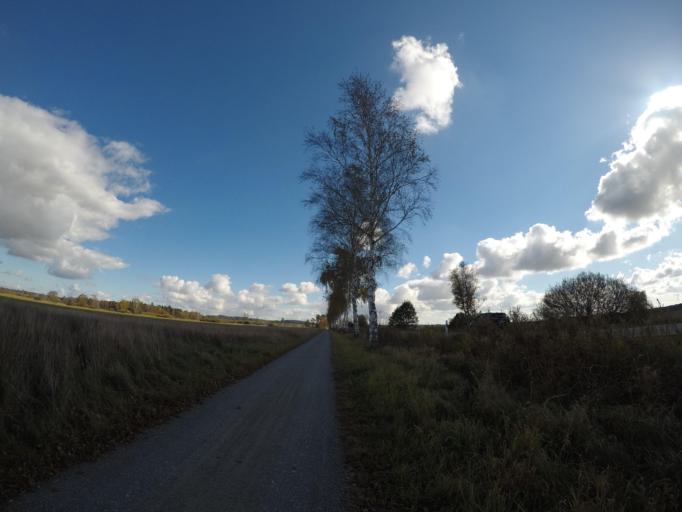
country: DE
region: Baden-Wuerttemberg
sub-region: Tuebingen Region
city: Bad Buchau
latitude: 48.0655
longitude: 9.6241
